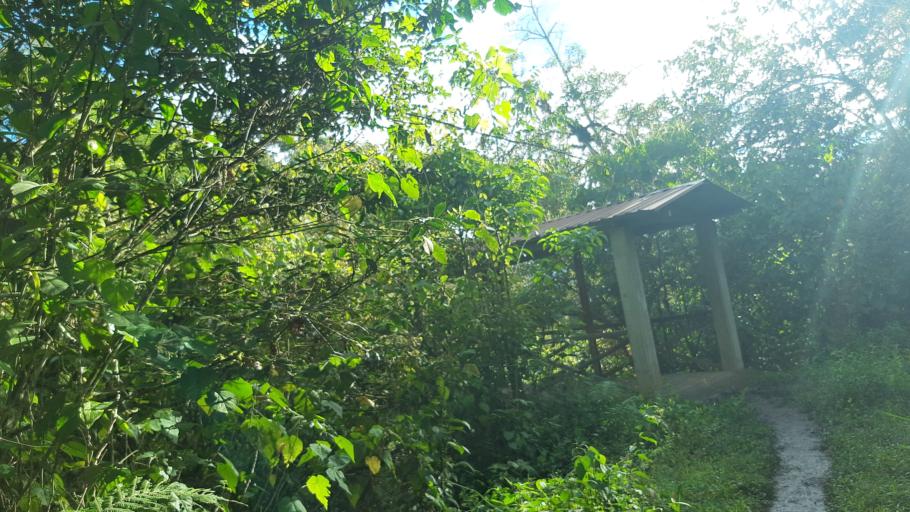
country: CO
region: Boyaca
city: Garagoa
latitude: 5.0951
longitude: -73.3566
